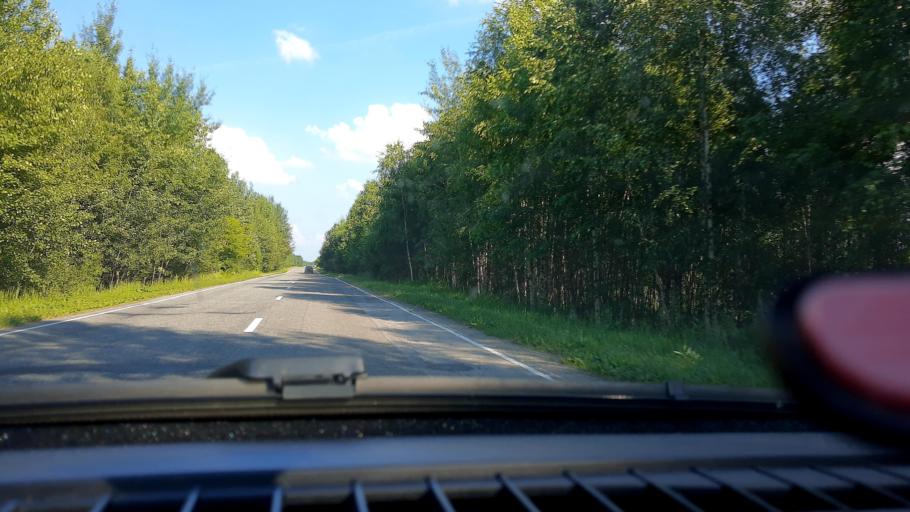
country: RU
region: Nizjnij Novgorod
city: Neklyudovo
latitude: 56.5086
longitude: 43.9638
